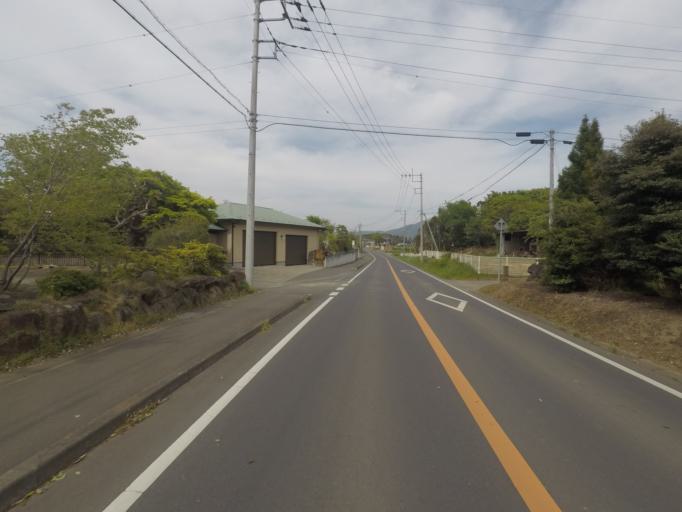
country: JP
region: Ibaraki
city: Makabe
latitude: 36.2720
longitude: 140.0707
